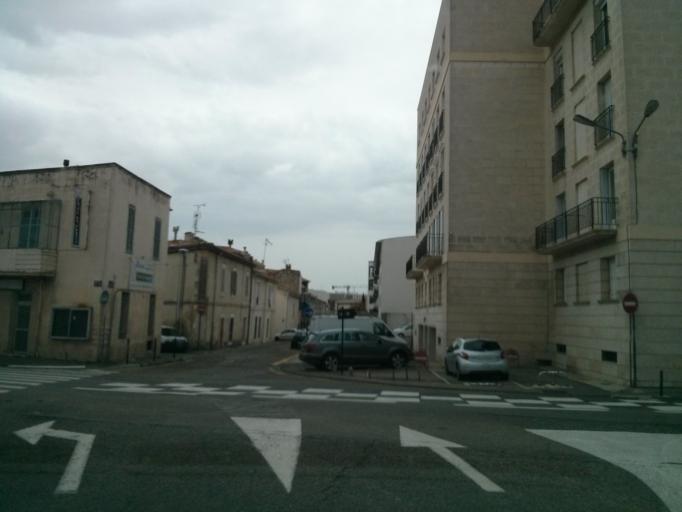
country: FR
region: Languedoc-Roussillon
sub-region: Departement du Gard
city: Nimes
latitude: 43.8322
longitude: 4.3528
